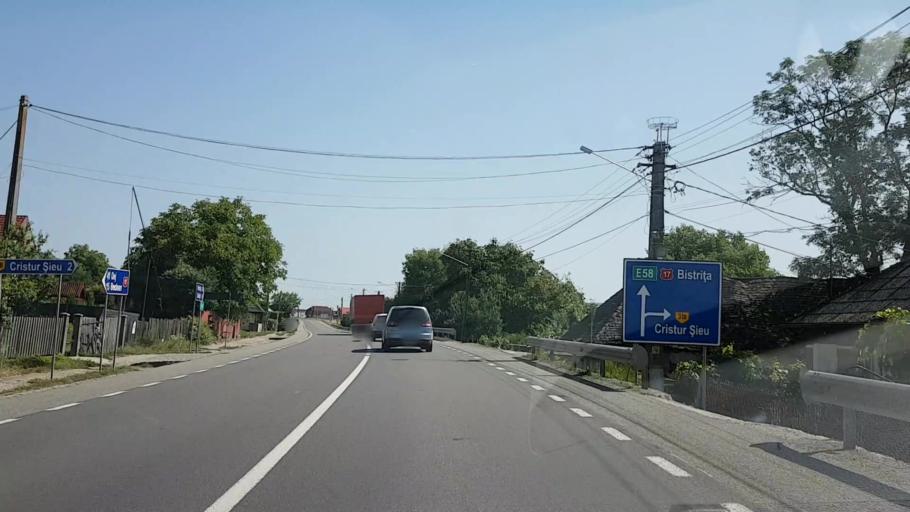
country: RO
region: Bistrita-Nasaud
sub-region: Comuna Sieu-Odorhei
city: Sieu-Odorhei
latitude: 47.1404
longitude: 24.3066
